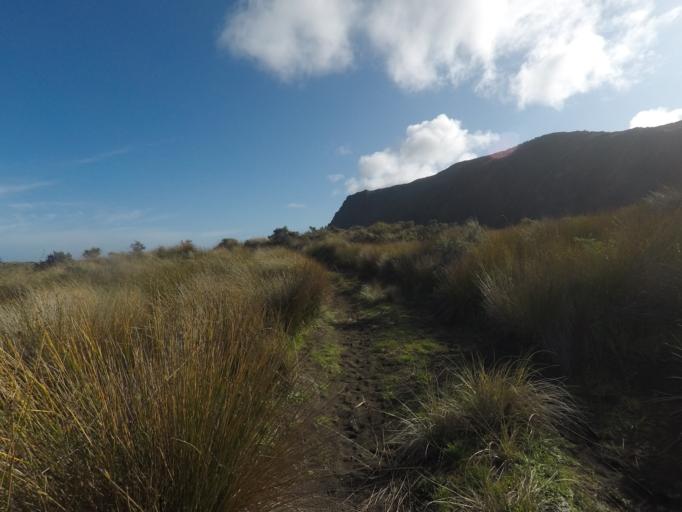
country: NZ
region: Auckland
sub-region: Auckland
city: Titirangi
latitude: -37.0089
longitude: 174.4810
